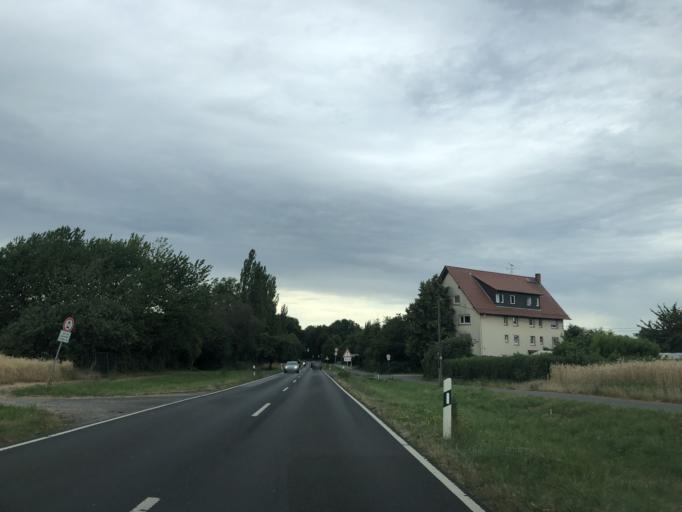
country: DE
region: Hesse
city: Dreieich
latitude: 50.0105
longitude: 8.7311
